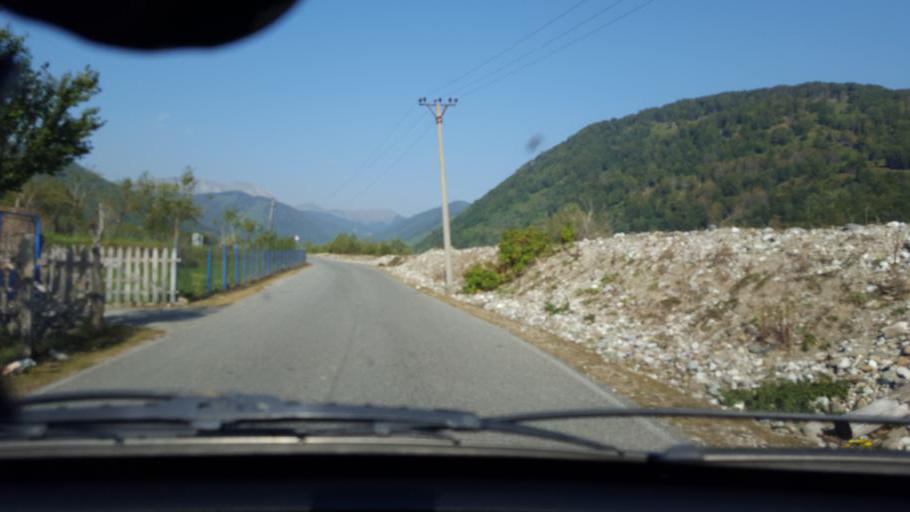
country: ME
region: Andrijevica
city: Andrijevica
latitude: 42.5889
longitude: 19.7005
